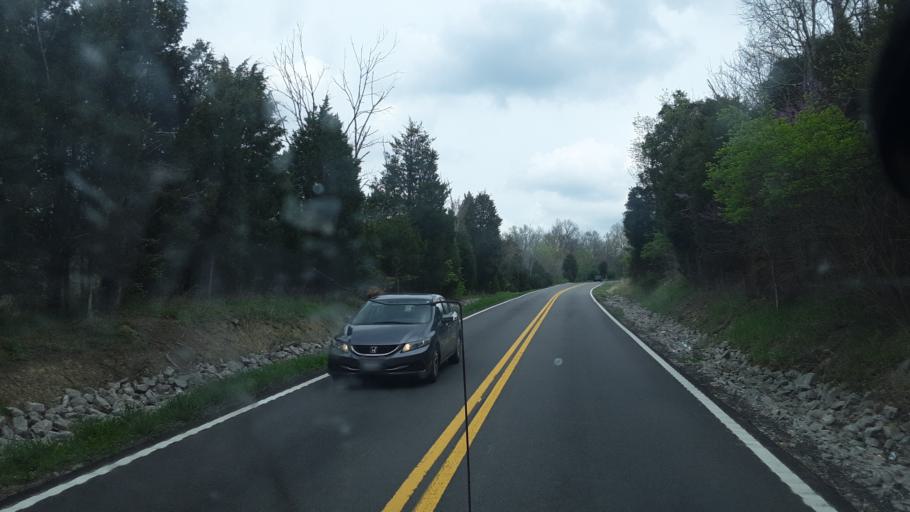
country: US
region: Kentucky
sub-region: Grant County
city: Dry Ridge
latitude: 38.6600
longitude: -84.6685
